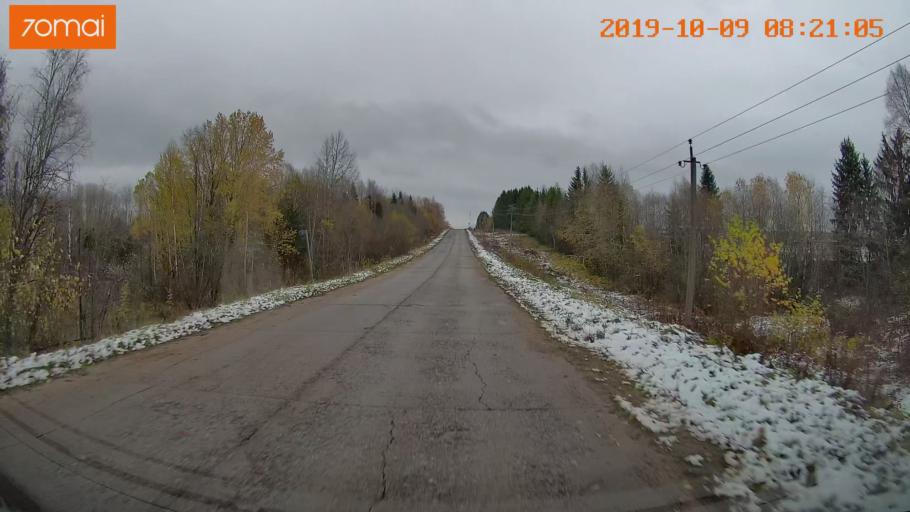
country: RU
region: Vologda
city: Gryazovets
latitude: 58.7423
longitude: 40.2708
